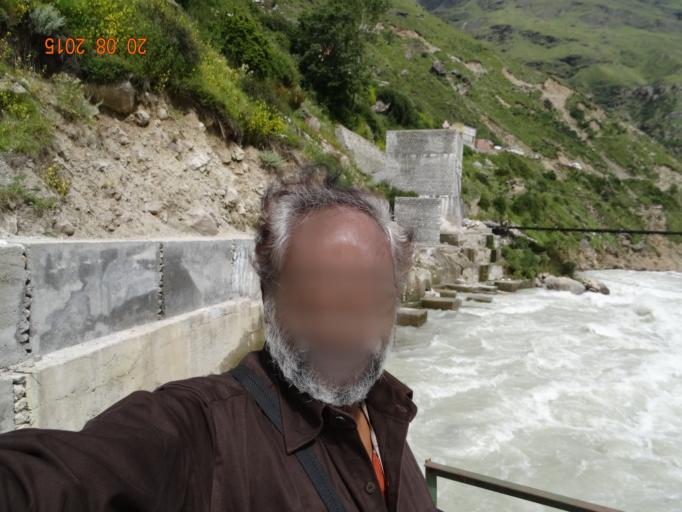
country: IN
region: Uttarakhand
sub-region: Chamoli
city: Joshimath
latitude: 30.7699
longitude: 79.4954
